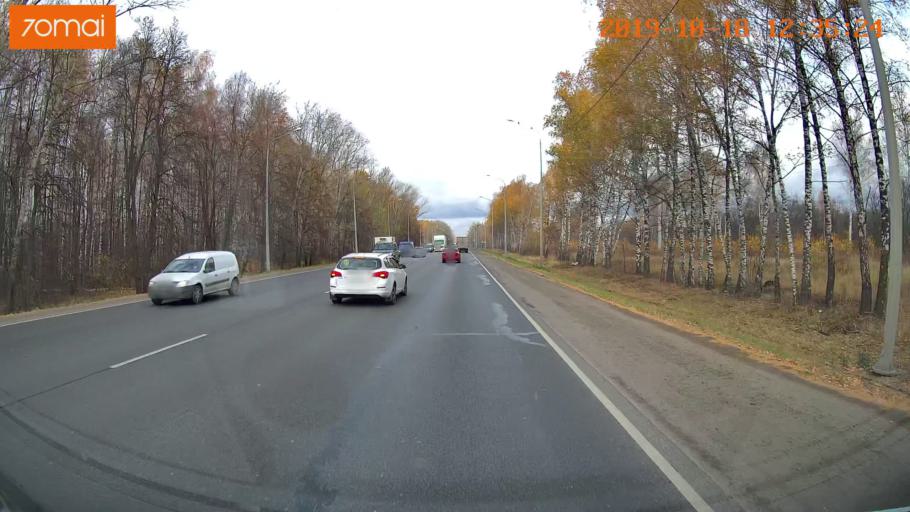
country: RU
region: Rjazan
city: Ryazan'
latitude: 54.6242
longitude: 39.6357
